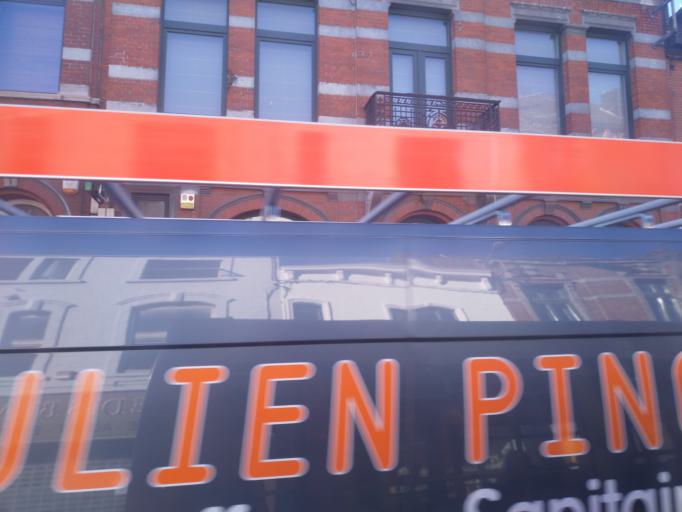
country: BE
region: Wallonia
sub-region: Province du Hainaut
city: Charleroi
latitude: 50.4008
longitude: 4.4475
